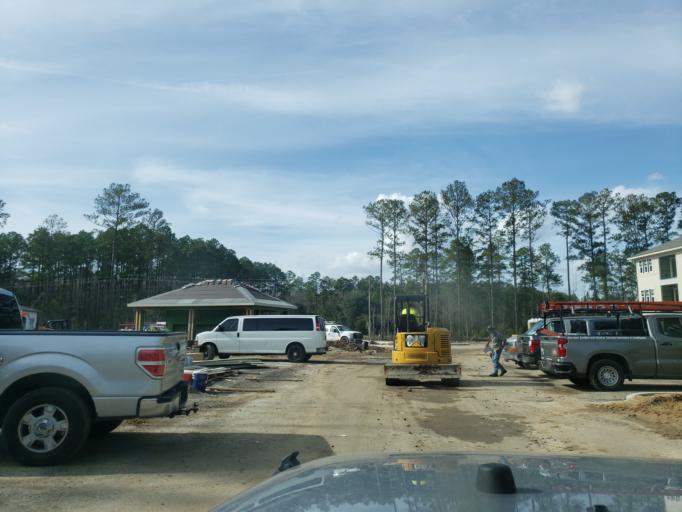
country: US
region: Georgia
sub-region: Chatham County
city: Pooler
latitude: 32.1710
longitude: -81.2325
